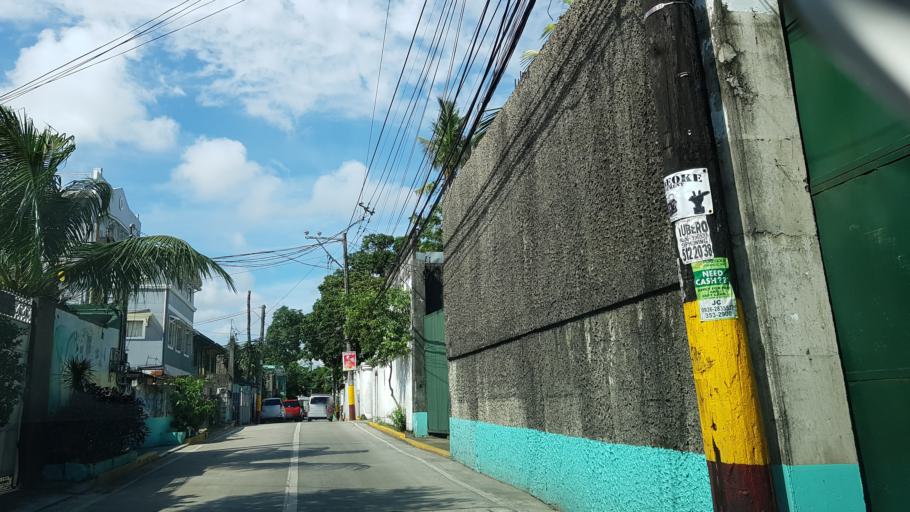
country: PH
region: Metro Manila
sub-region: Mandaluyong
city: Mandaluyong City
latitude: 14.5824
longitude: 121.0176
